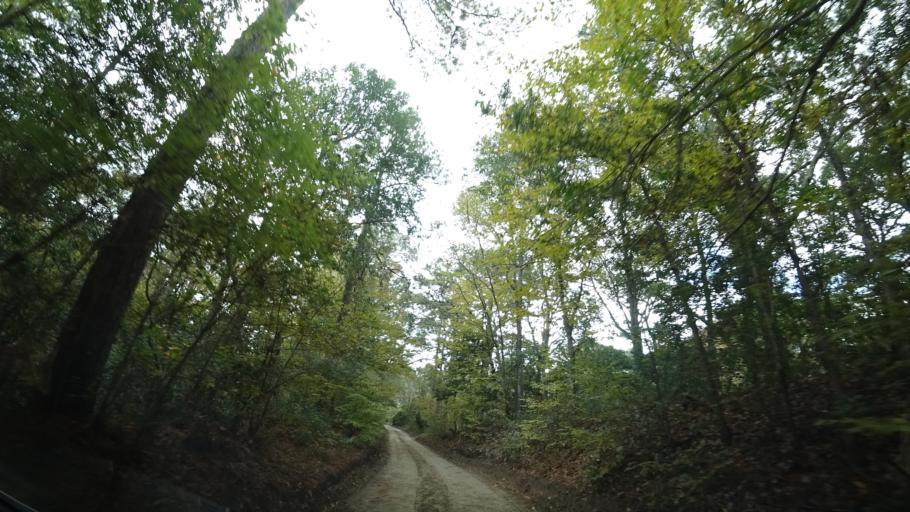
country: US
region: North Carolina
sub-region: Dare County
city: Kill Devil Hills
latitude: 35.9948
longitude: -75.6664
